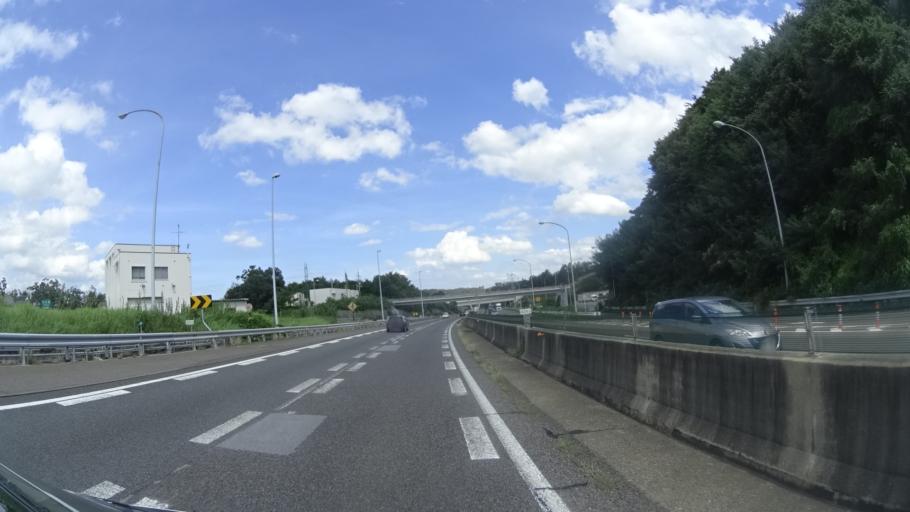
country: JP
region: Shiga Prefecture
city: Youkaichi
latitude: 35.1630
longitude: 136.2752
